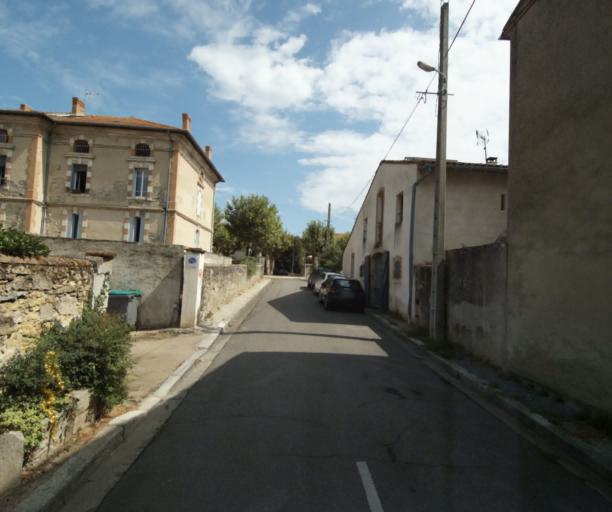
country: FR
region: Midi-Pyrenees
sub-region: Departement de la Haute-Garonne
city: Revel
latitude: 43.4605
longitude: 2.0005
